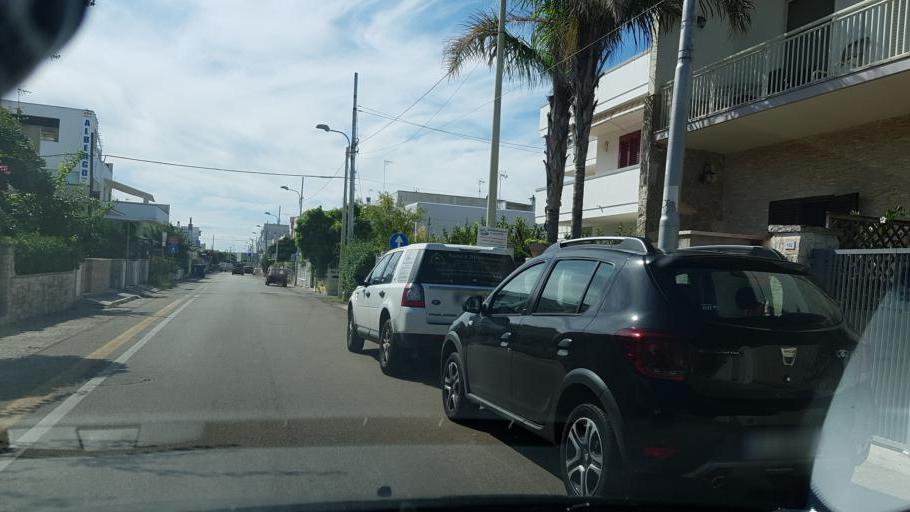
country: IT
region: Apulia
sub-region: Provincia di Lecce
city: Borgagne
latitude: 40.2760
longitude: 18.4288
